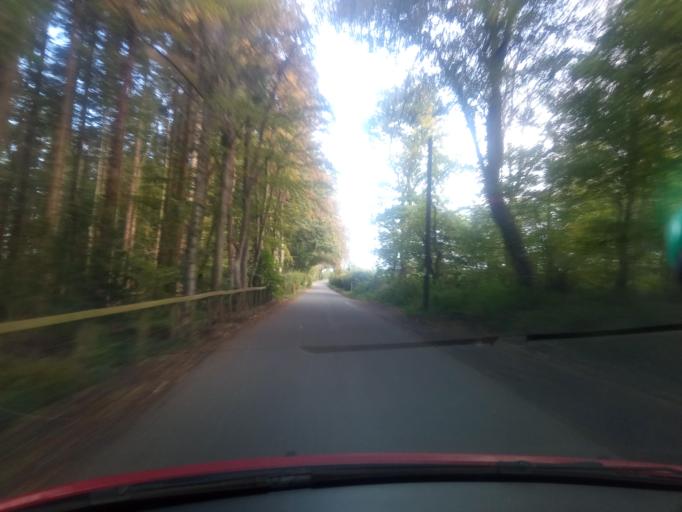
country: GB
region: Scotland
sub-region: The Scottish Borders
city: Jedburgh
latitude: 55.3774
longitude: -2.6475
